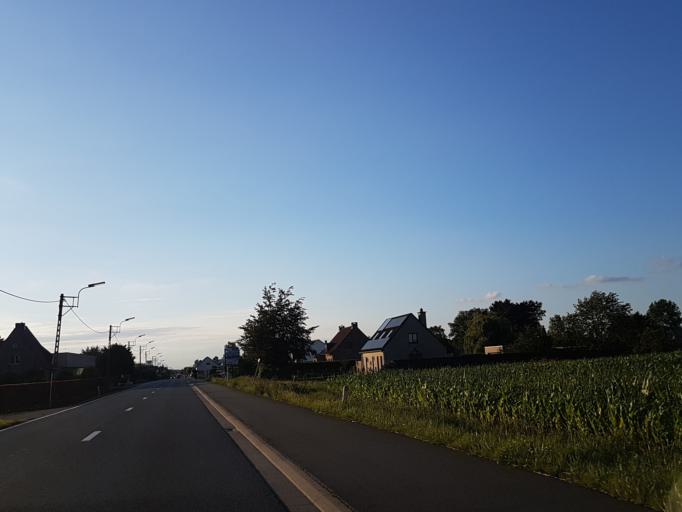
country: BE
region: Flanders
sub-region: Provincie Oost-Vlaanderen
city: Lebbeke
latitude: 50.9728
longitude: 4.1477
